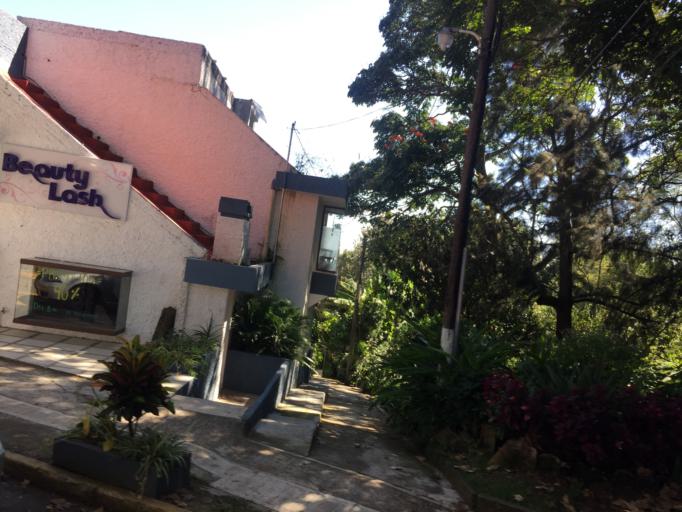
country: MX
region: Veracruz
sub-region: Xalapa
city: Xalapa de Enriquez
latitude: 19.5333
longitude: -96.8924
